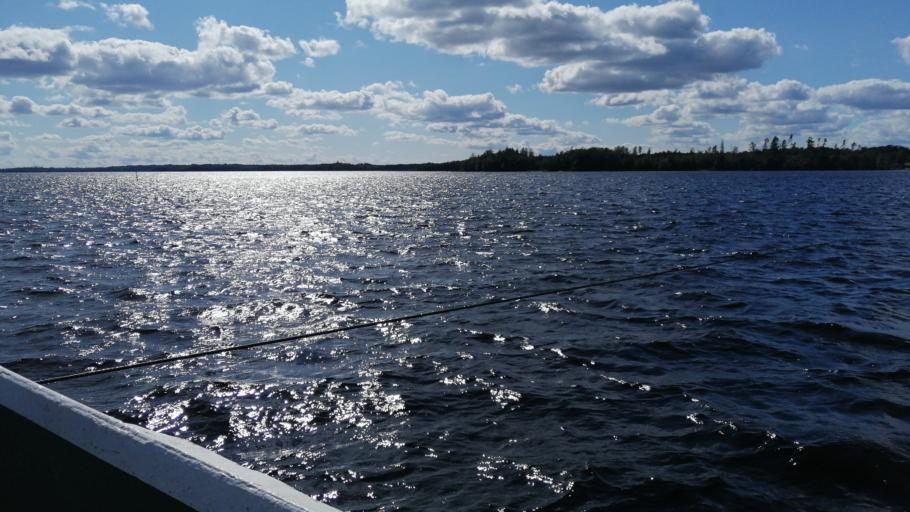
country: SE
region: Joenkoeping
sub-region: Varnamo Kommun
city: Bredaryd
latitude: 57.0068
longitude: 13.7169
